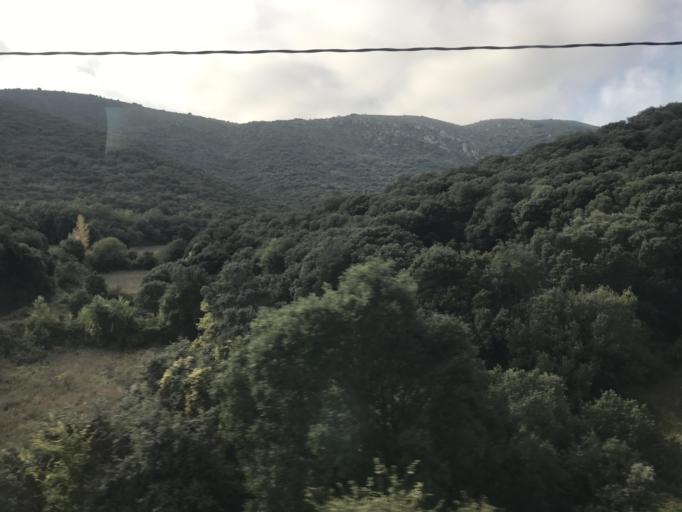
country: ES
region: Castille and Leon
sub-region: Provincia de Burgos
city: Ameyugo
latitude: 42.6486
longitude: -3.0731
